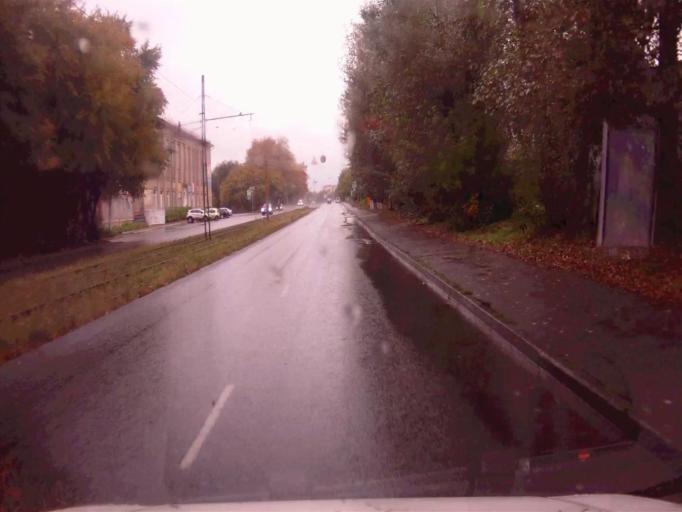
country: RU
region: Chelyabinsk
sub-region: Gorod Chelyabinsk
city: Chelyabinsk
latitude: 55.1797
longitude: 61.4147
